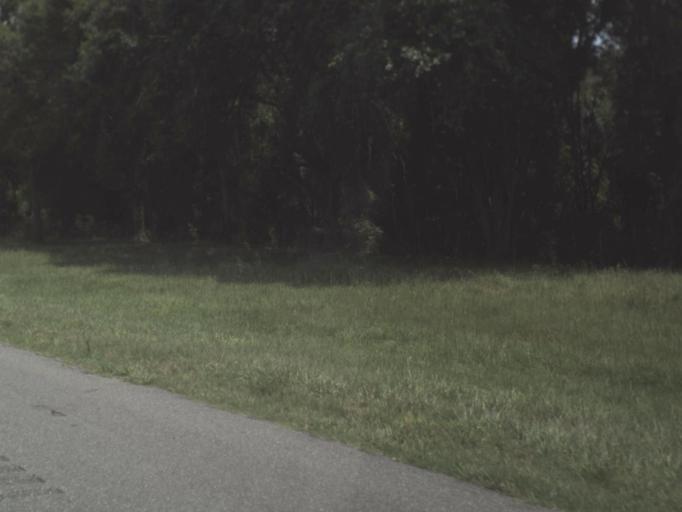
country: US
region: Florida
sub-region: Hamilton County
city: Jasper
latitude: 30.4883
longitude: -83.0136
